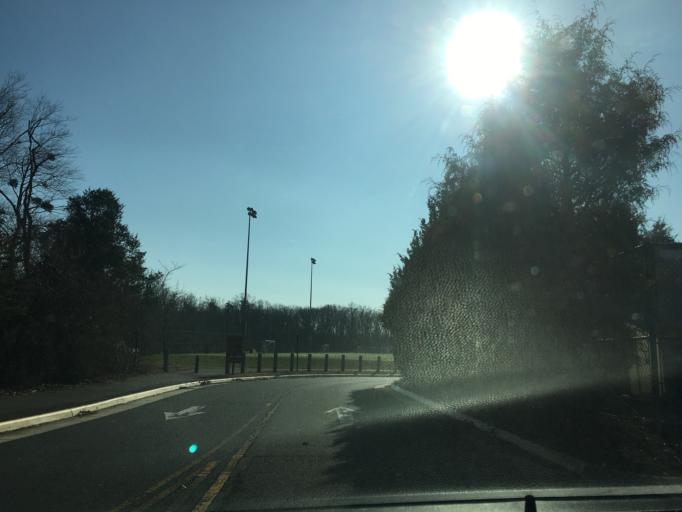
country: US
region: Virginia
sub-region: Fairfax County
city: Fairfax Station
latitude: 38.8284
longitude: -77.3642
